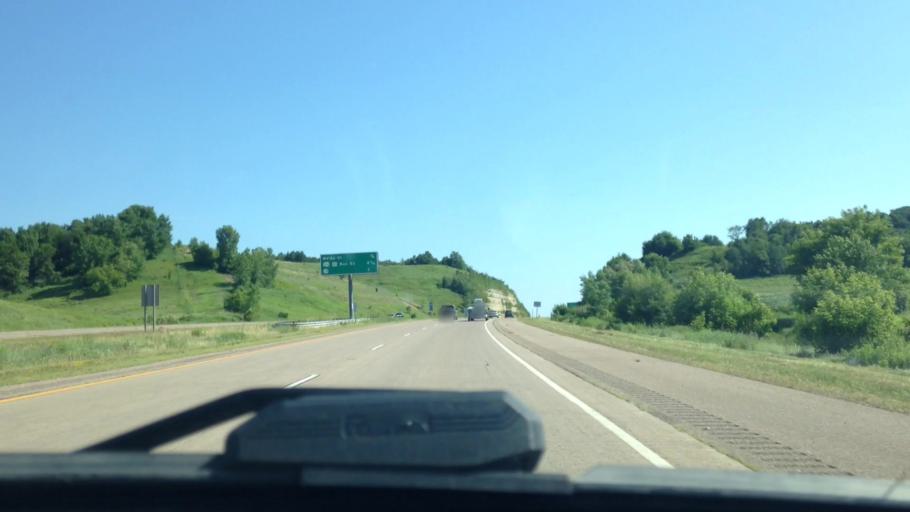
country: US
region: Wisconsin
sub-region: Eau Claire County
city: Seymour
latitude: 44.8481
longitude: -91.4387
